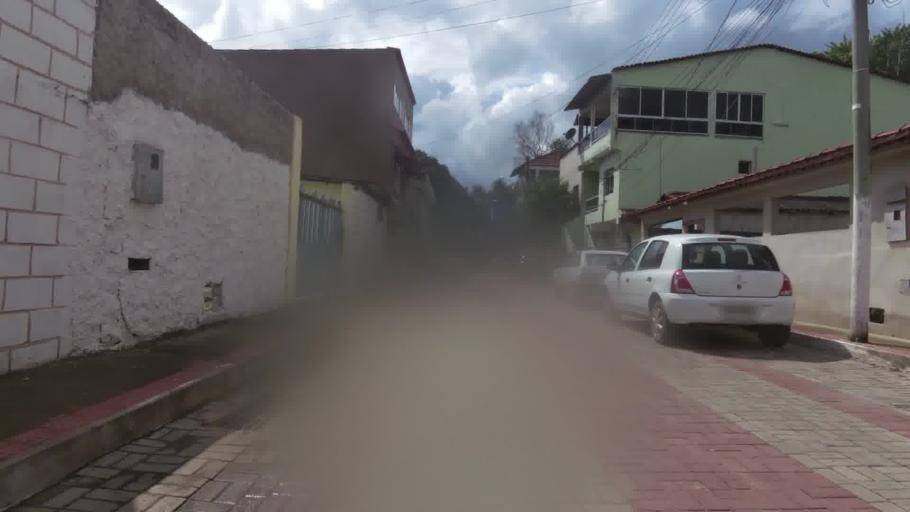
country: BR
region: Espirito Santo
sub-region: Piuma
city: Piuma
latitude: -20.8028
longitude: -40.6546
